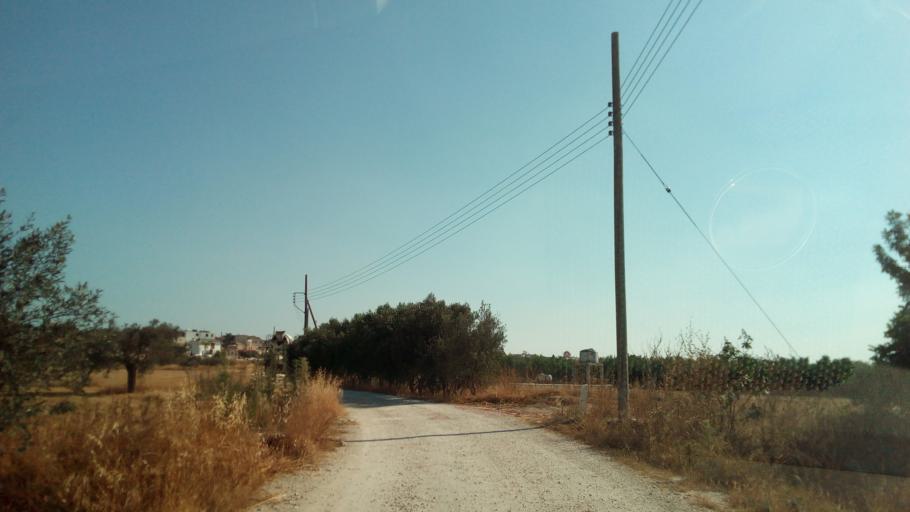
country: CY
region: Larnaka
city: Aradippou
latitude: 34.9580
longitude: 33.5963
